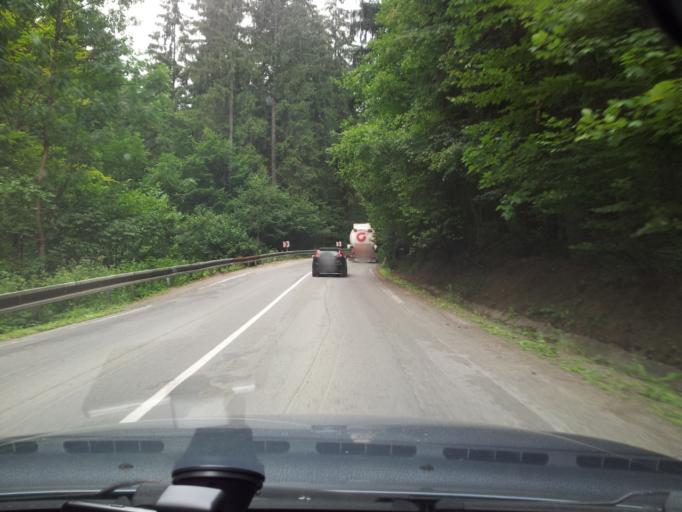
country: SK
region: Zilinsky
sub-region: Okres Dolny Kubin
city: Dolny Kubin
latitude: 49.2862
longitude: 19.3495
